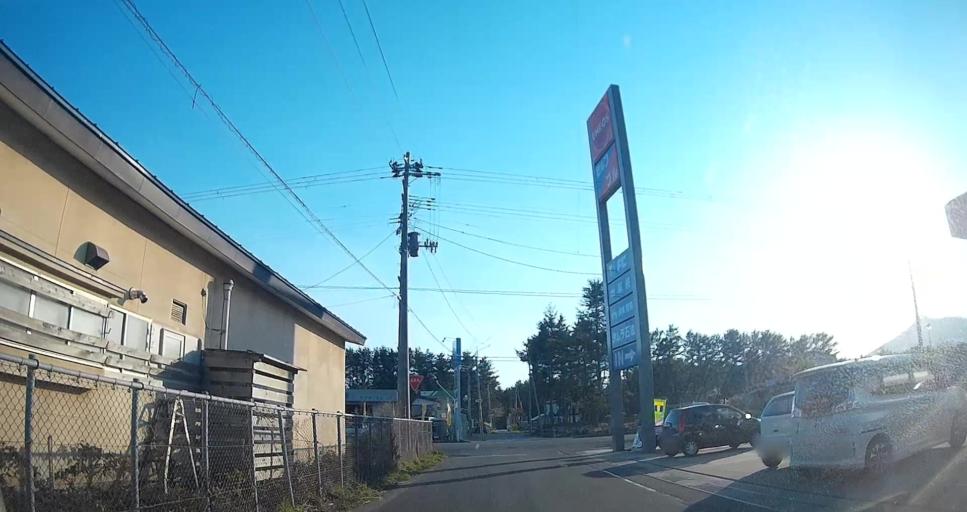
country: JP
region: Aomori
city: Mutsu
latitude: 41.2638
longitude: 141.2162
